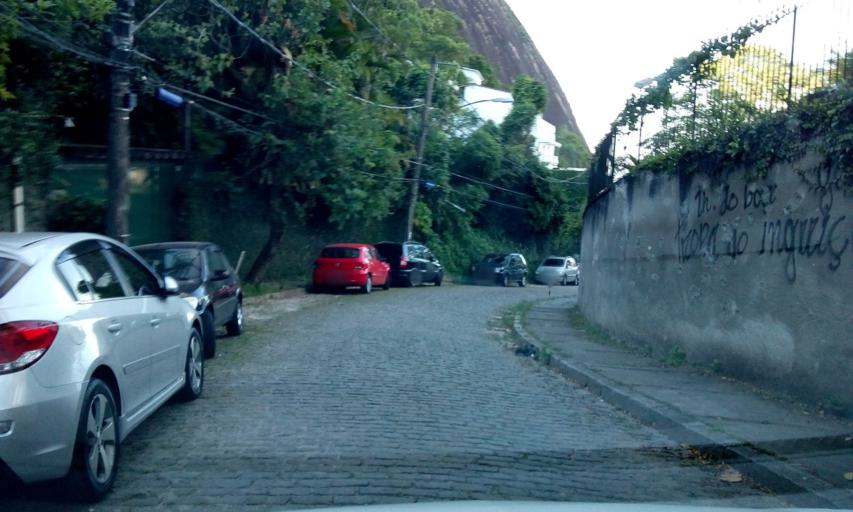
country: BR
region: Rio de Janeiro
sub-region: Rio De Janeiro
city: Rio de Janeiro
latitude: -22.9651
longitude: -43.1975
